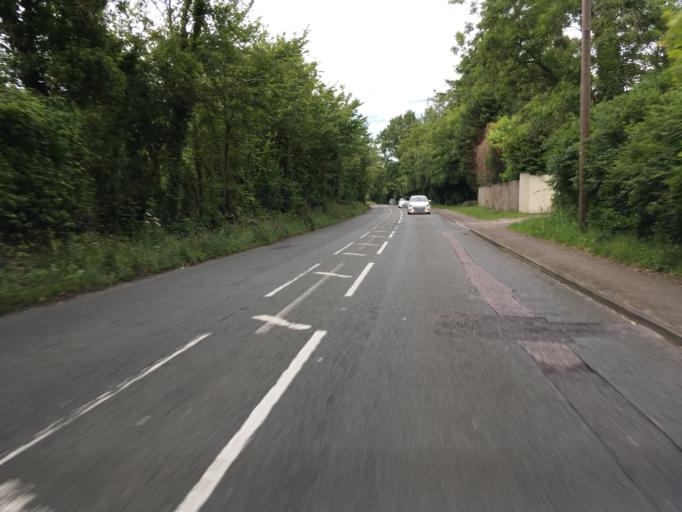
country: GB
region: England
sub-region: Oxfordshire
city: Oxford
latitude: 51.7251
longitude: -1.2646
